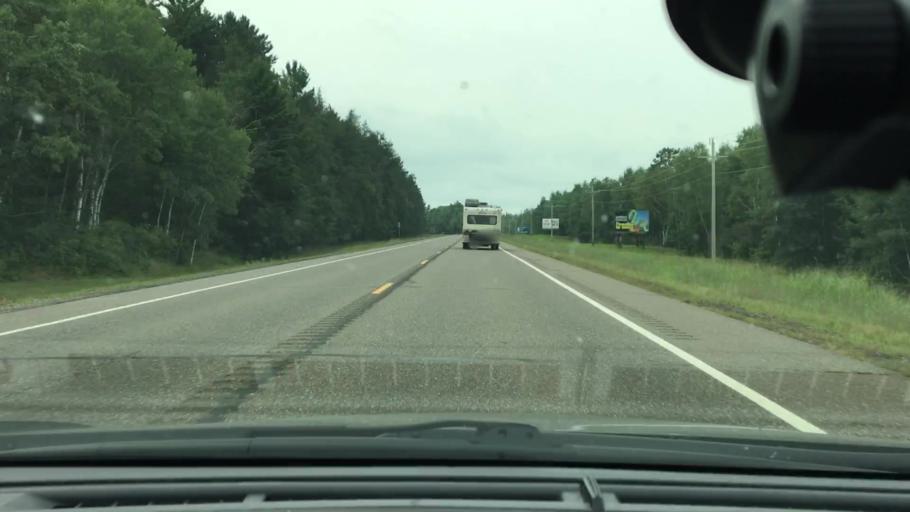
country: US
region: Minnesota
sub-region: Crow Wing County
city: Crosby
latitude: 46.5010
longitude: -93.9572
